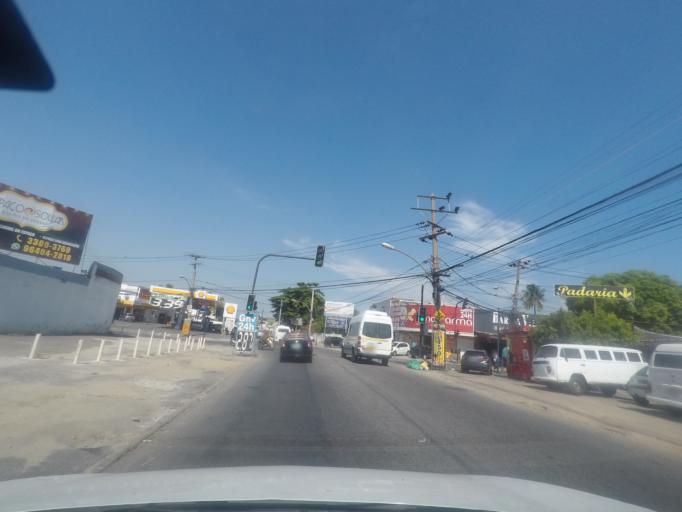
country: BR
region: Rio de Janeiro
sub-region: Nilopolis
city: Nilopolis
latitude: -22.8794
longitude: -43.4517
